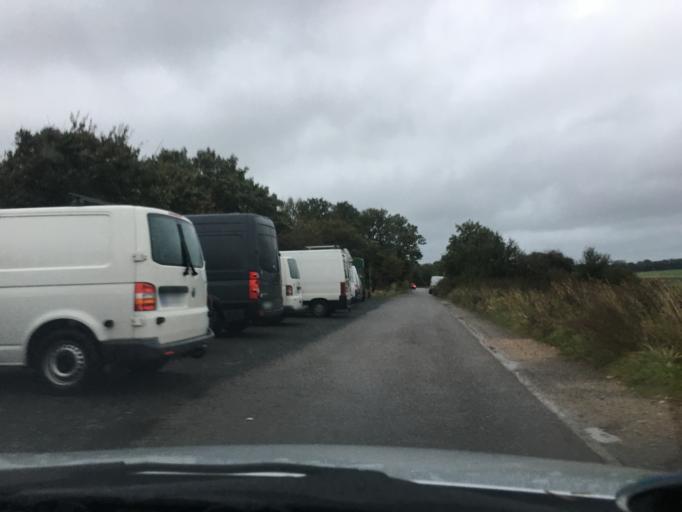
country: DE
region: Schleswig-Holstein
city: Strande
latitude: 54.4498
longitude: 10.1944
